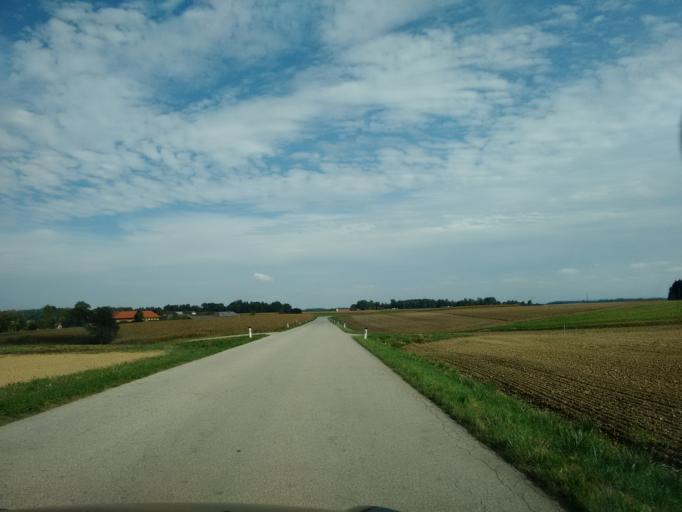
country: AT
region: Upper Austria
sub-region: Wels-Land
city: Marchtrenk
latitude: 48.1271
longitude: 14.1026
